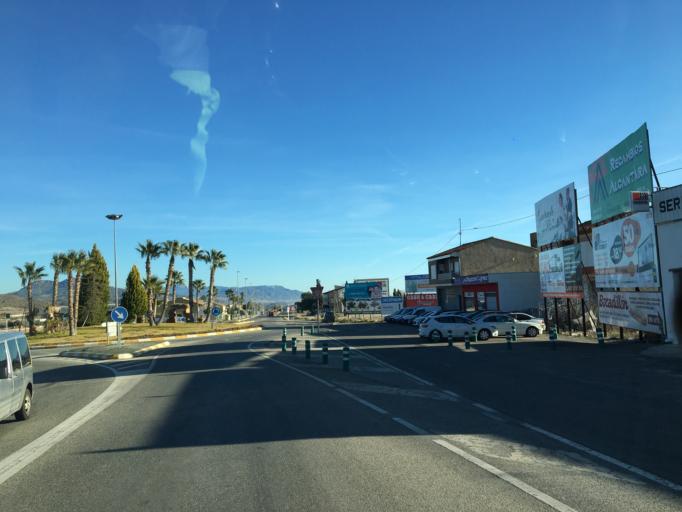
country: ES
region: Murcia
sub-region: Murcia
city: Puerto Lumbreras
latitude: 37.5735
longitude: -1.7969
